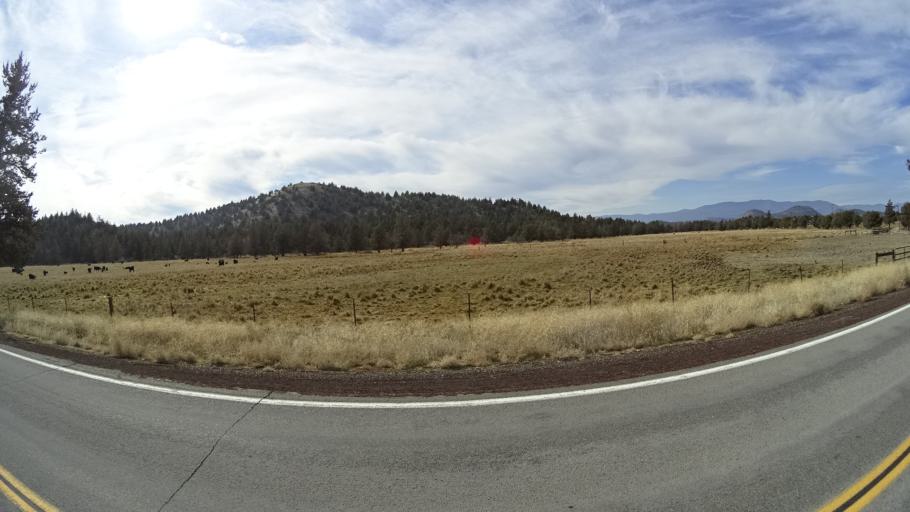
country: US
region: California
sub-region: Siskiyou County
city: Weed
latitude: 41.5803
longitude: -122.3985
